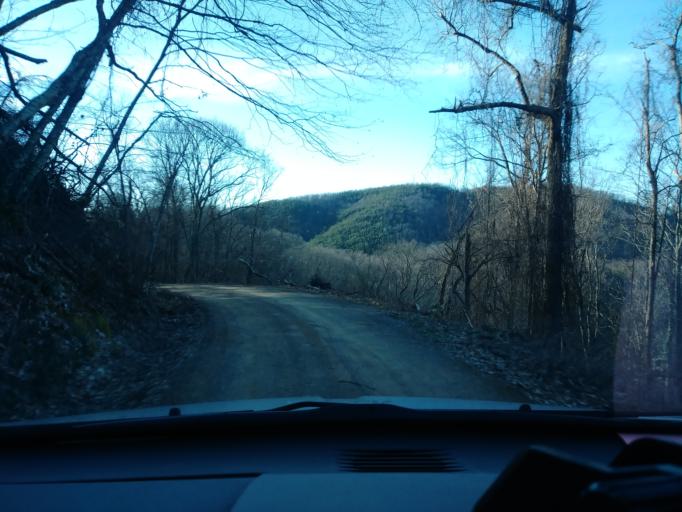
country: US
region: Tennessee
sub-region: Greene County
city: Tusculum
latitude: 36.0689
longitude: -82.6843
